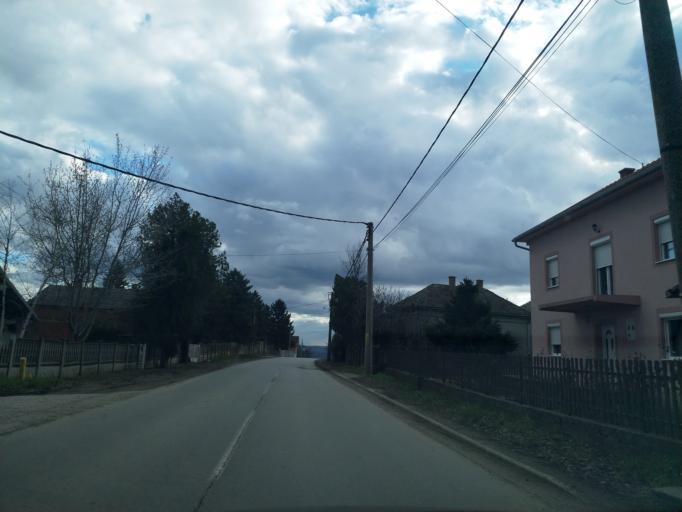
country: RS
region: Central Serbia
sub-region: Belgrade
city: Grocka
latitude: 44.6054
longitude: 20.7255
